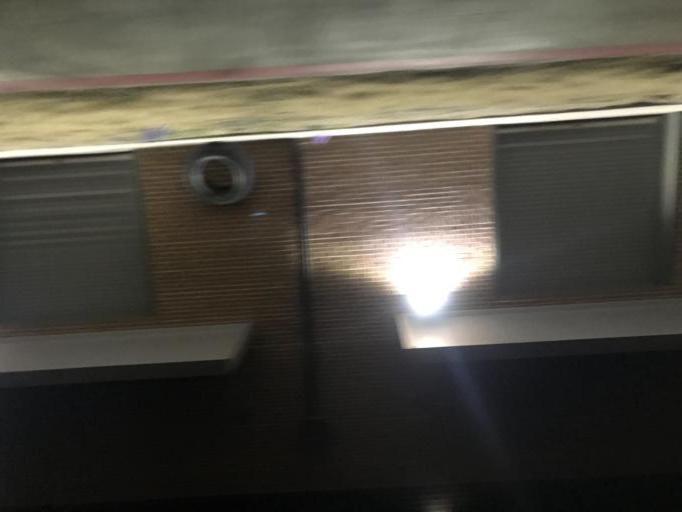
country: US
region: Texas
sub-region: Taylor County
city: Potosi
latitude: 32.3749
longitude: -99.7162
